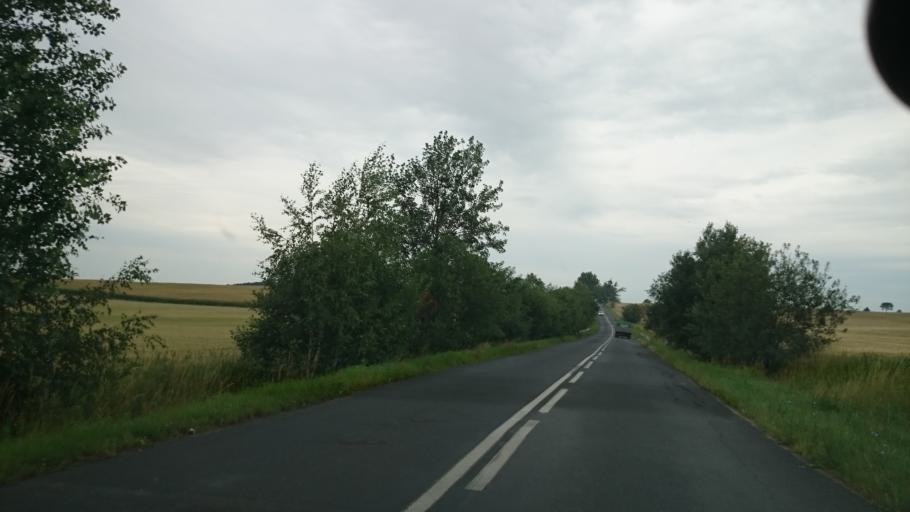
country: PL
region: Lower Silesian Voivodeship
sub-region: Powiat strzelinski
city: Przeworno
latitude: 50.6599
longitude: 17.2574
